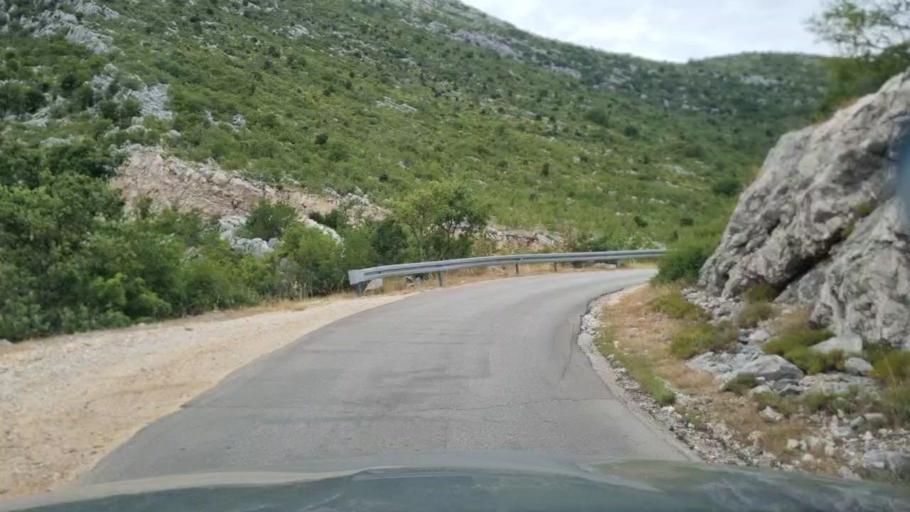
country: HR
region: Dubrovacko-Neretvanska
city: Podgora
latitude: 42.9671
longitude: 17.7949
